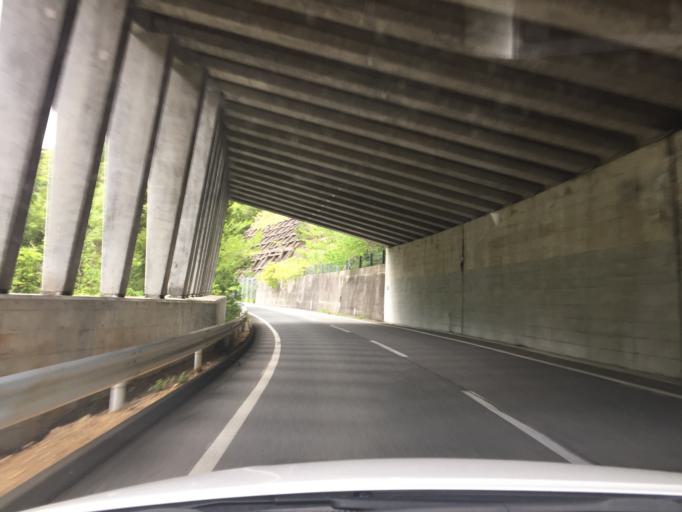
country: JP
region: Miyagi
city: Marumori
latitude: 37.7155
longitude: 140.8436
